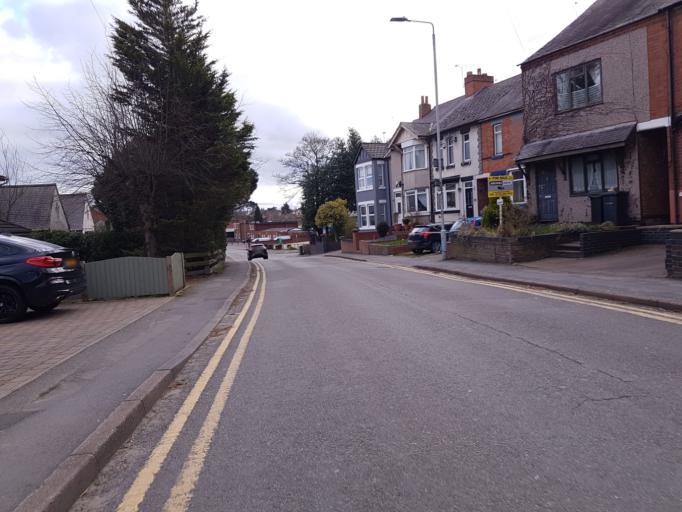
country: GB
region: England
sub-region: Leicestershire
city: Earl Shilton
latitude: 52.5751
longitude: -1.3161
